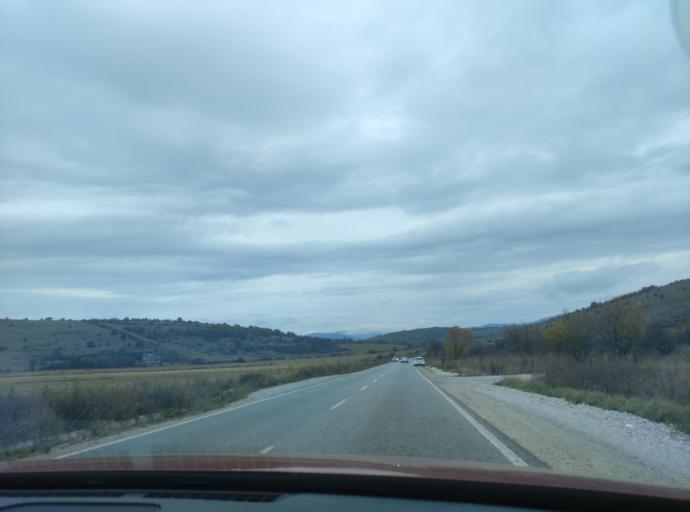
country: BG
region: Sofiya
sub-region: Obshtina Godech
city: Godech
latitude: 42.9523
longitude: 23.1578
